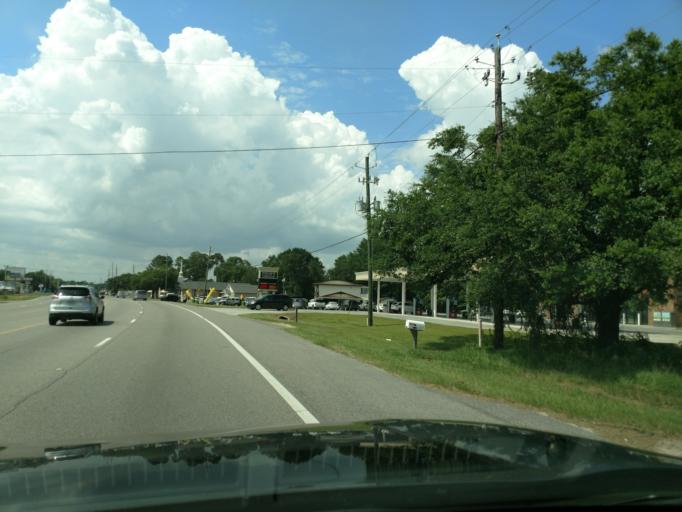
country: US
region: Mississippi
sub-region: Jackson County
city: Gulf Hills
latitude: 30.4287
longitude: -88.8292
